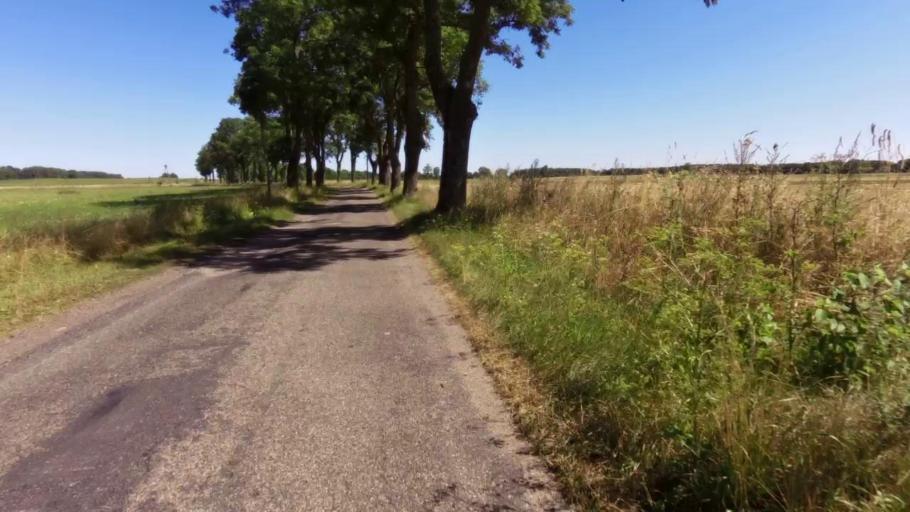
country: PL
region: West Pomeranian Voivodeship
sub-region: Powiat szczecinecki
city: Lubowo
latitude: 53.5585
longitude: 16.3273
